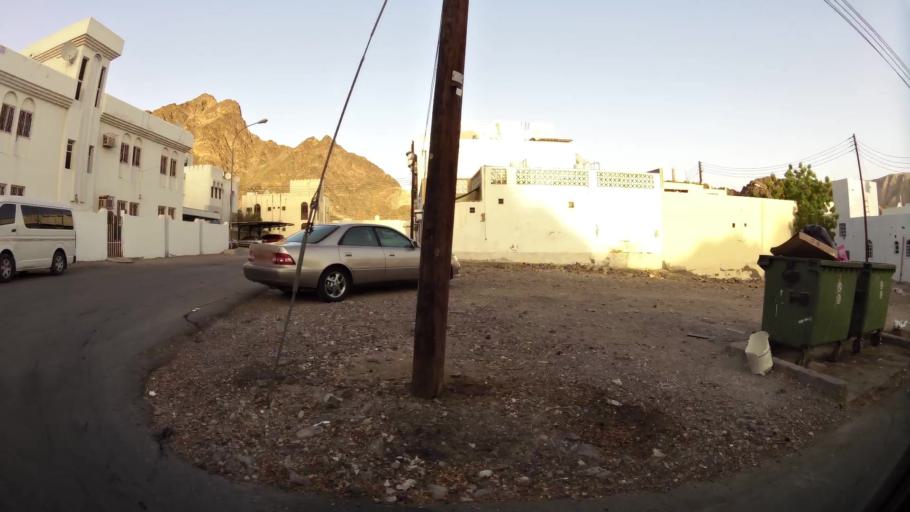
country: OM
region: Muhafazat Masqat
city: Muscat
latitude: 23.5764
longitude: 58.5750
